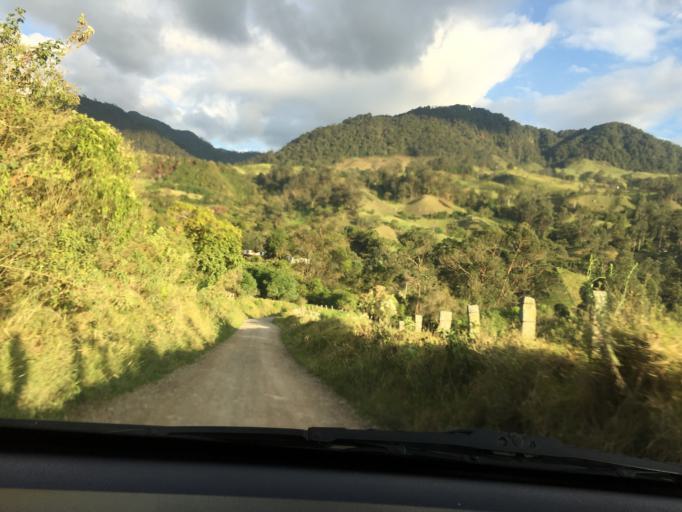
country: CO
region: Cundinamarca
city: Zipacon
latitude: 4.7236
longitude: -74.3891
